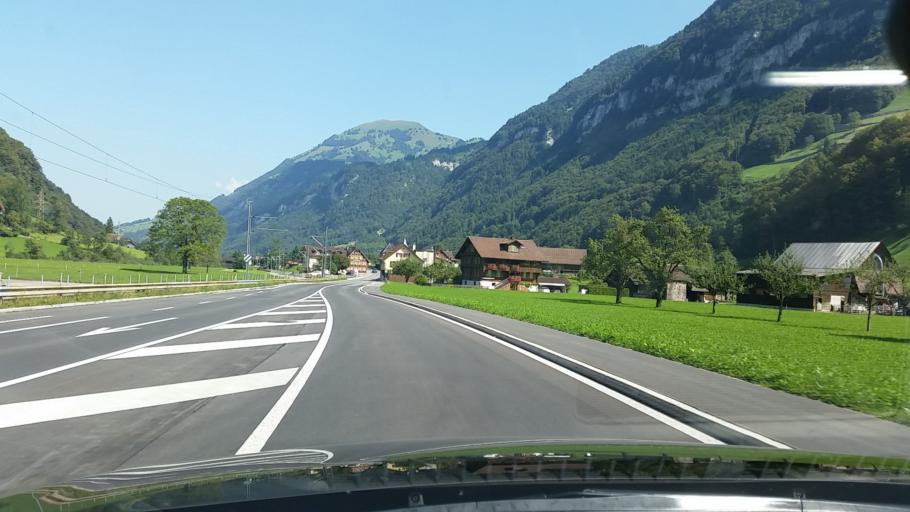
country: CH
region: Nidwalden
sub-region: Nidwalden
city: Wolfenschiessen
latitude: 46.8946
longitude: 8.3889
